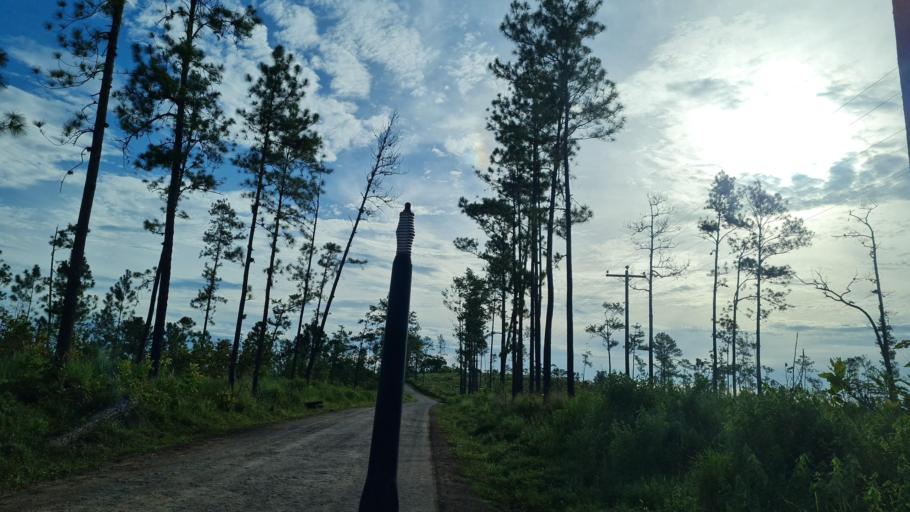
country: NI
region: Atlantico Sur
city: La Cruz de Rio Grande
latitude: 13.5564
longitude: -84.2964
